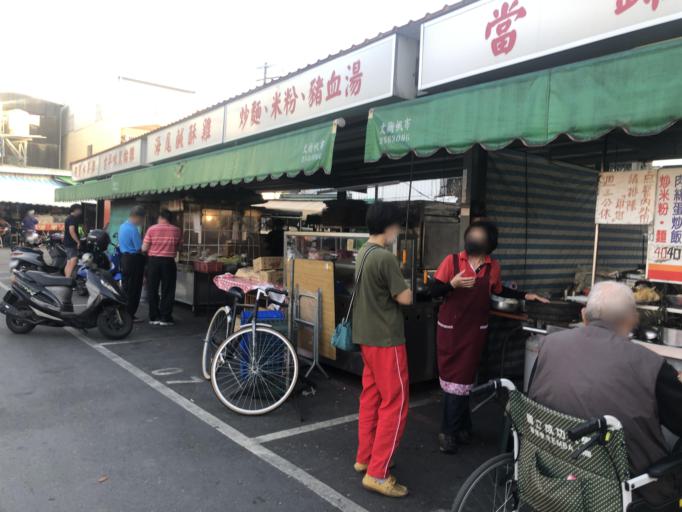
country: TW
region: Taiwan
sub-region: Tainan
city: Tainan
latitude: 23.0402
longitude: 120.1841
